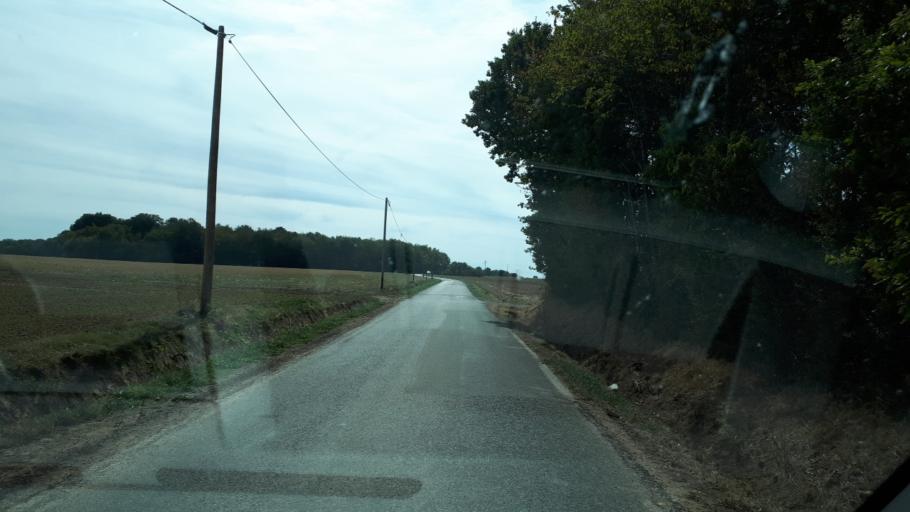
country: FR
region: Centre
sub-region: Departement du Loir-et-Cher
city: Montoire-sur-le-Loir
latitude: 47.6993
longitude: 0.8317
